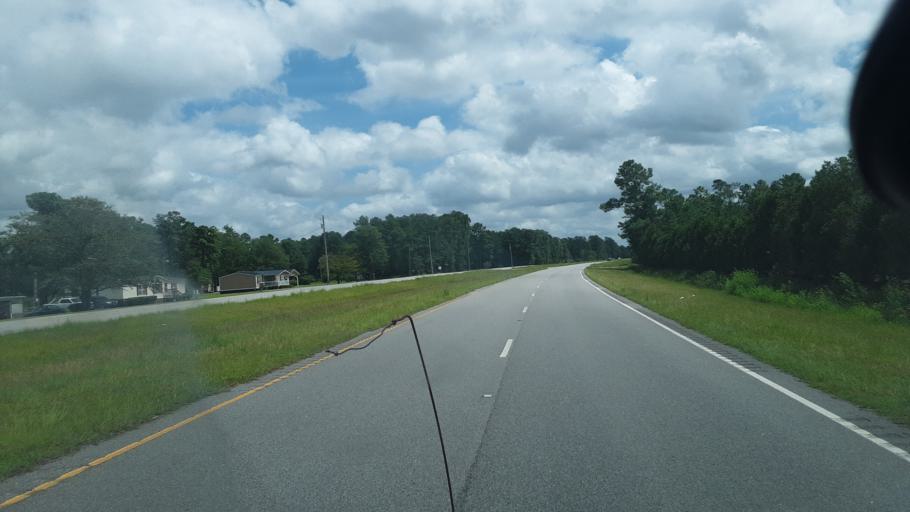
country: US
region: South Carolina
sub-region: Horry County
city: Loris
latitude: 34.1065
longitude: -78.9320
